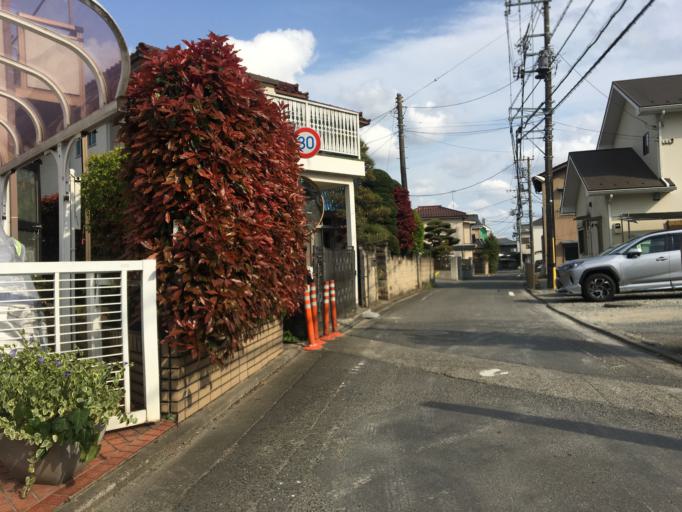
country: JP
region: Tokyo
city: Chofugaoka
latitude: 35.6478
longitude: 139.5019
